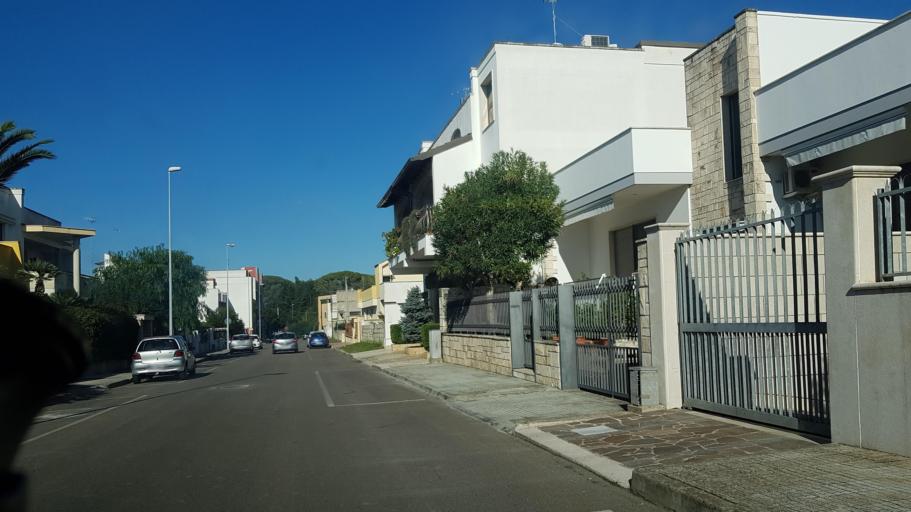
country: IT
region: Apulia
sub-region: Provincia di Lecce
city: Arnesano
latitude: 40.3303
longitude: 18.1012
